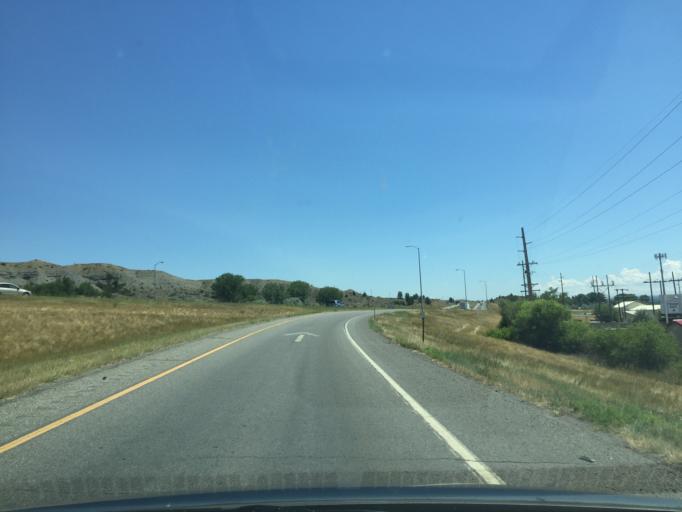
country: US
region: Montana
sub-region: Stillwater County
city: Columbus
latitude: 45.6456
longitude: -109.2467
